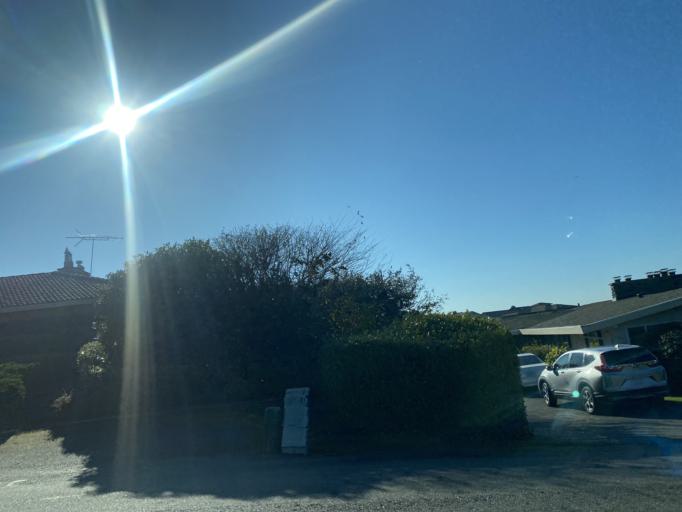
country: US
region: Washington
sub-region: King County
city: Shoreline
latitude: 47.7557
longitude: -122.3725
